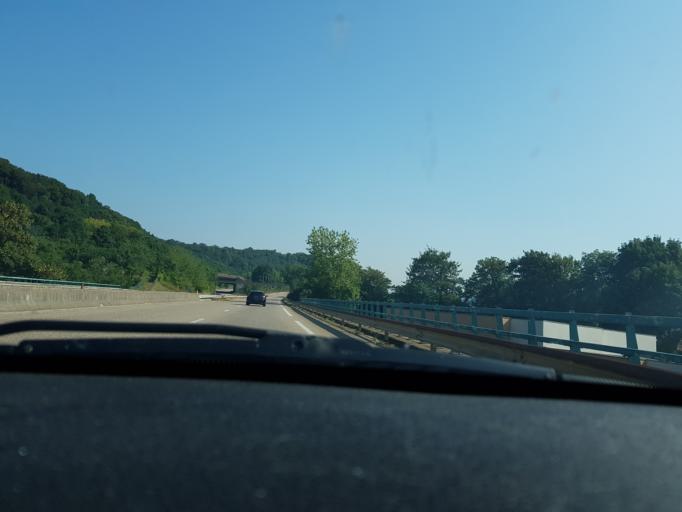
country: FR
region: Lorraine
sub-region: Departement de Meurthe-et-Moselle
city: Maxeville
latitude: 48.7131
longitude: 6.1617
